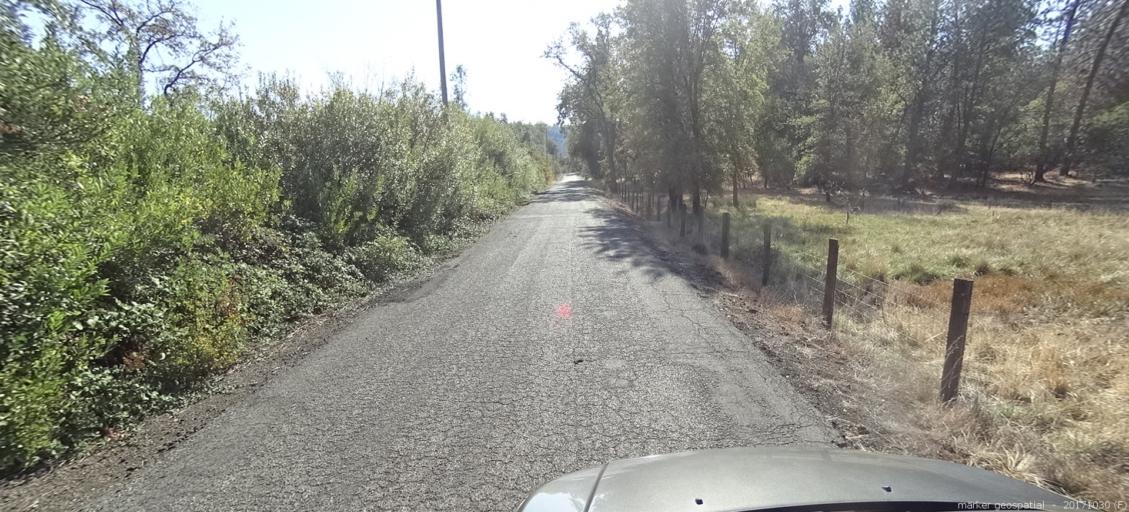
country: US
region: California
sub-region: Shasta County
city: Shingletown
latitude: 40.5220
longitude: -121.9644
